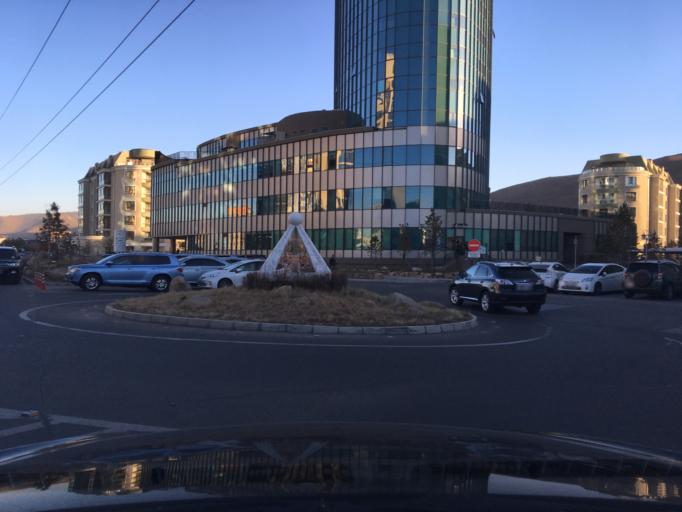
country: MN
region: Ulaanbaatar
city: Ulaanbaatar
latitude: 47.8903
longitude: 106.9319
